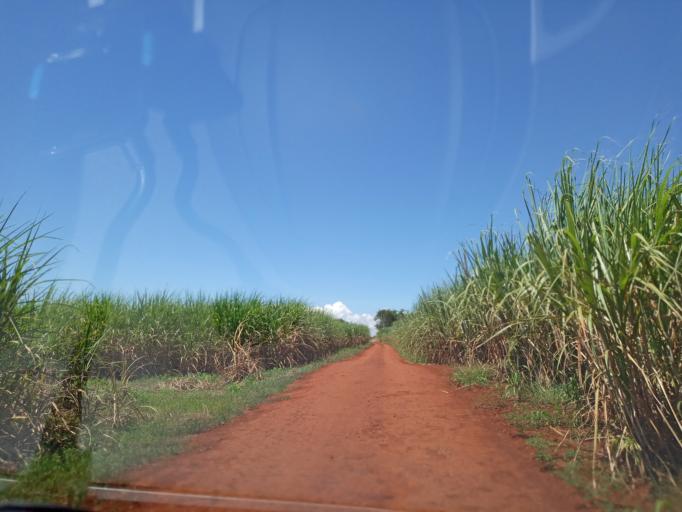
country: BR
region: Goias
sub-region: Itumbiara
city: Itumbiara
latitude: -18.4077
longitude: -49.1275
